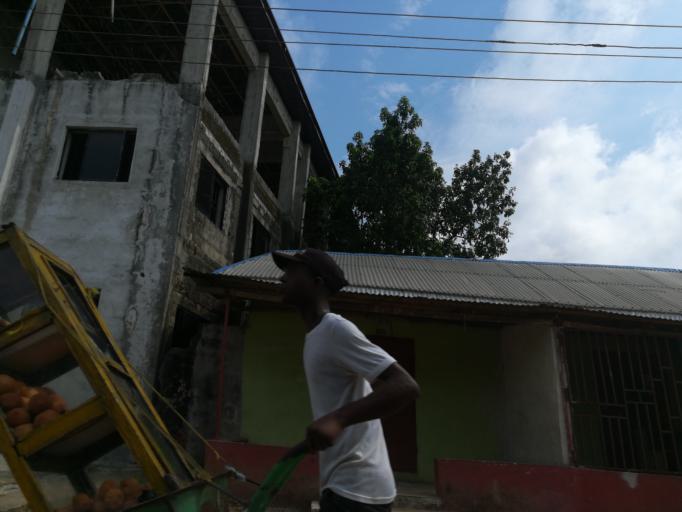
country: NG
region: Rivers
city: Okrika
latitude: 4.7501
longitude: 7.1054
